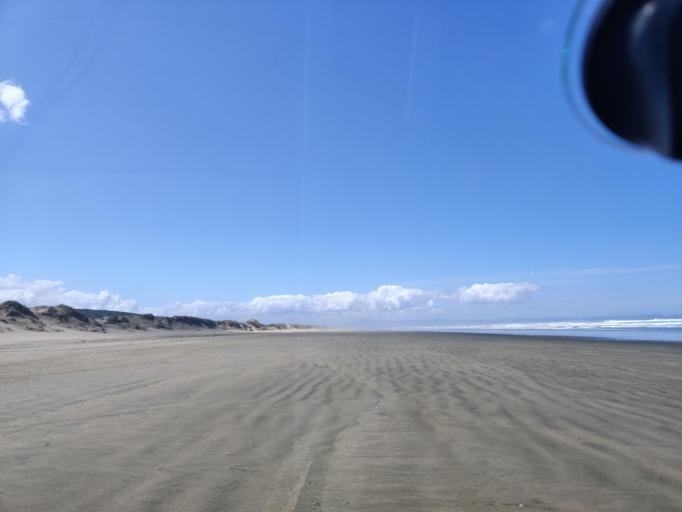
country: NZ
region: Northland
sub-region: Far North District
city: Kaitaia
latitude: -34.9520
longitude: 173.1230
